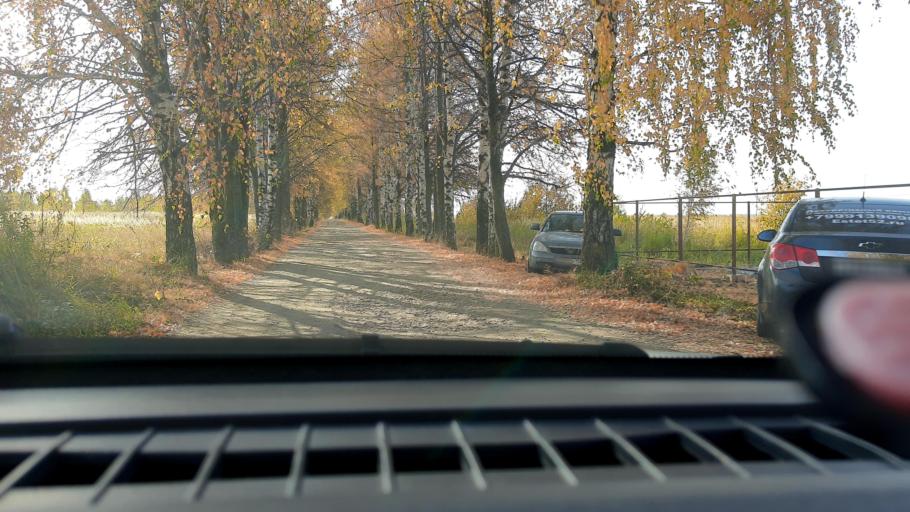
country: RU
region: Nizjnij Novgorod
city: Kstovo
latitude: 56.1520
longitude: 44.2818
